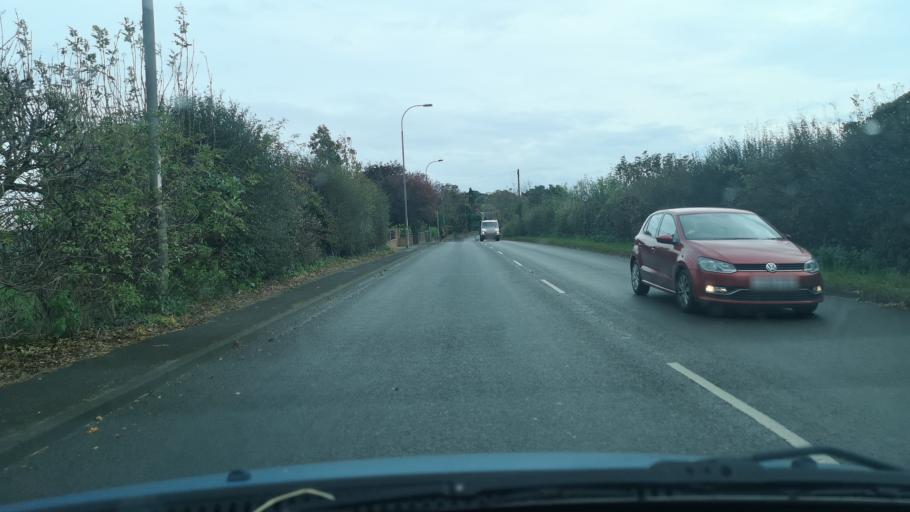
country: GB
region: England
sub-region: City and Borough of Wakefield
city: Sharlston
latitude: 53.6563
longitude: -1.4035
